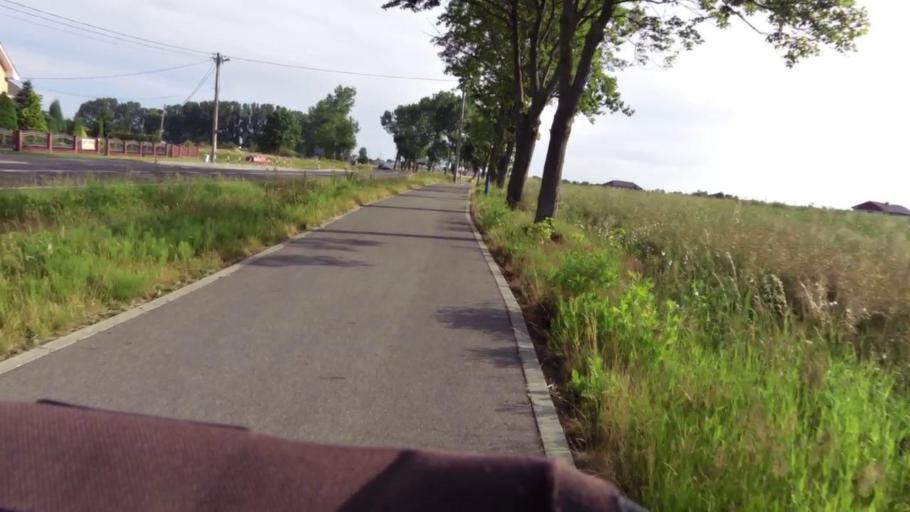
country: PL
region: West Pomeranian Voivodeship
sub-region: Powiat kamienski
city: Kamien Pomorski
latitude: 54.0027
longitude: 14.8171
